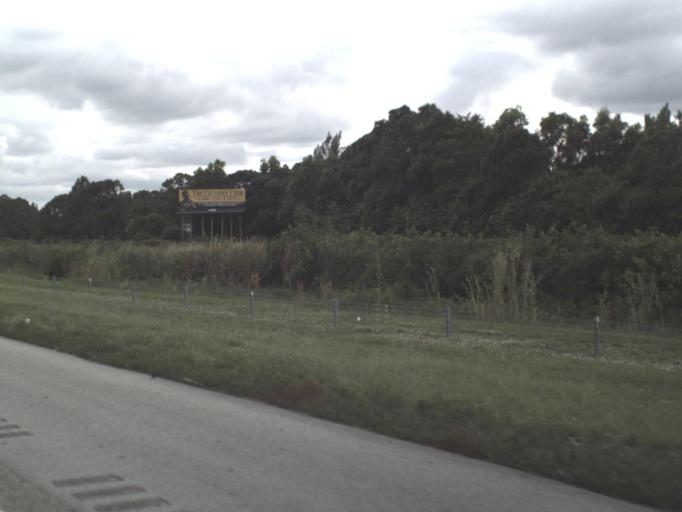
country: US
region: Florida
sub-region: Palm Beach County
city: Limestone Creek
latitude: 26.9091
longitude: -80.1426
